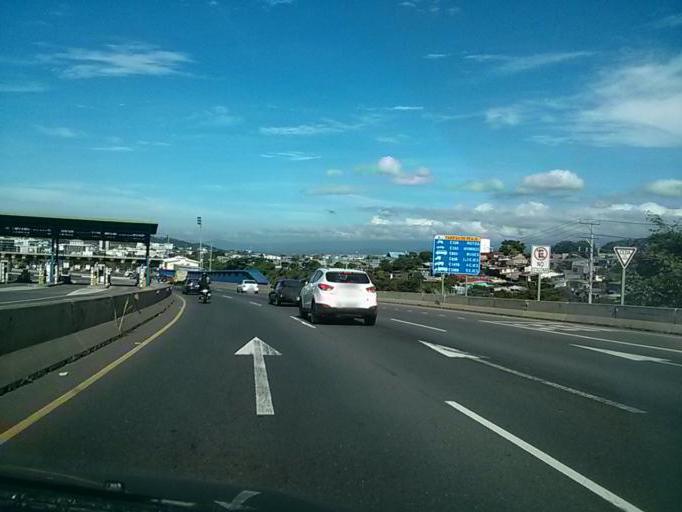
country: CR
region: San Jose
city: San Rafael
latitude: 9.9369
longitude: -84.1327
